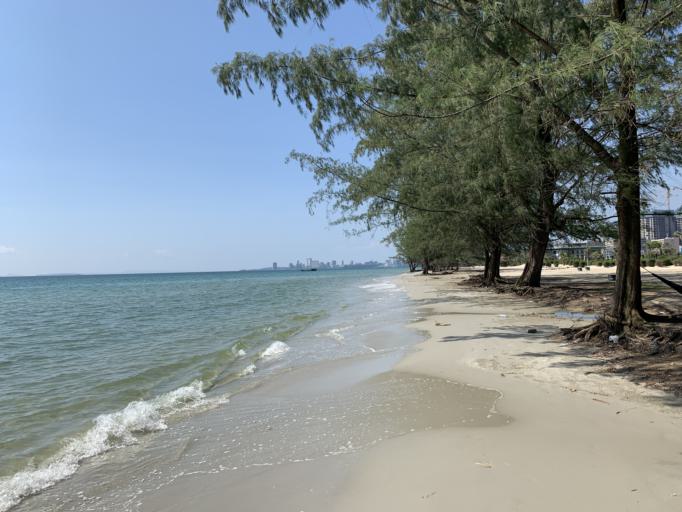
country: KH
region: Preah Sihanouk
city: Sihanoukville
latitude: 10.5624
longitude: 103.5570
